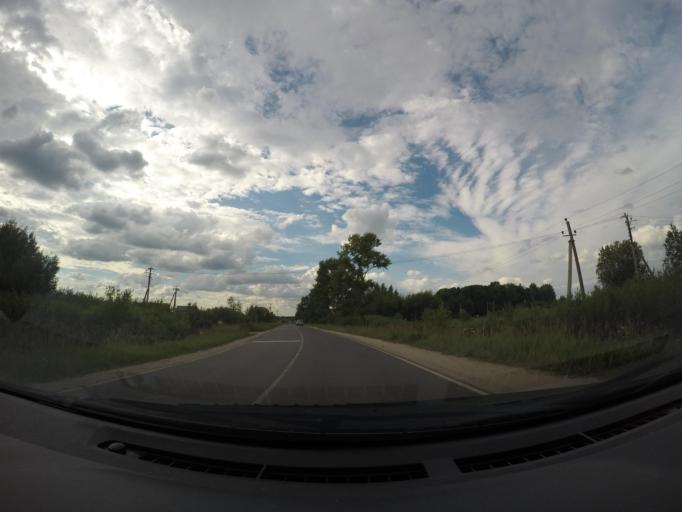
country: RU
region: Moskovskaya
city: Rechitsy
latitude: 55.6050
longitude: 38.5288
